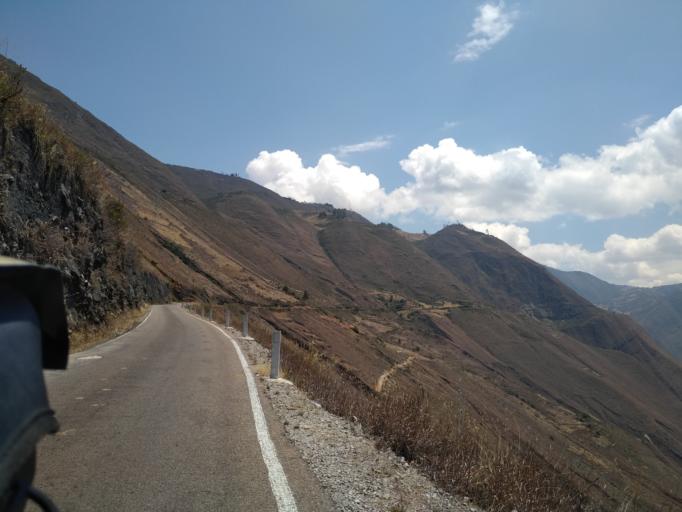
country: PE
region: Cajamarca
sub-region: Provincia de Celendin
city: Celendin
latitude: -6.8883
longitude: -78.0973
